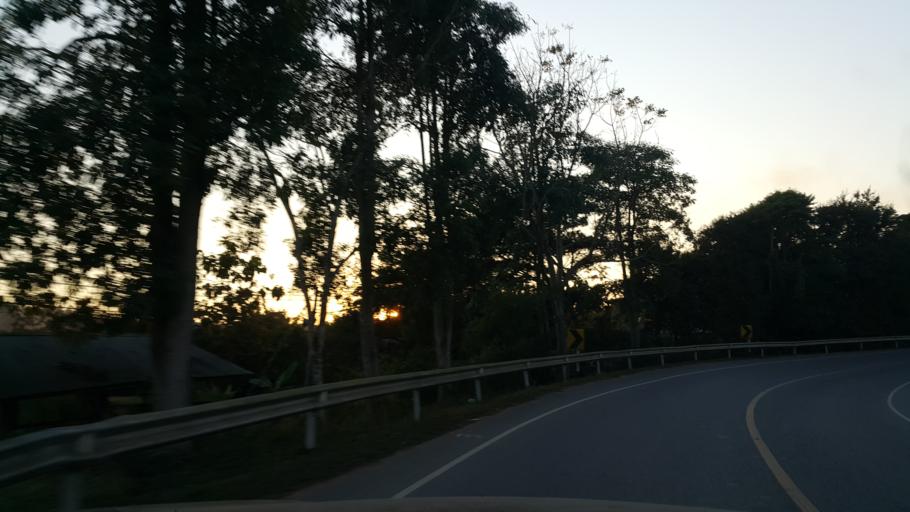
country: TH
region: Phrae
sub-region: Amphoe Wang Chin
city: Wang Chin
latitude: 17.8455
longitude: 99.6303
